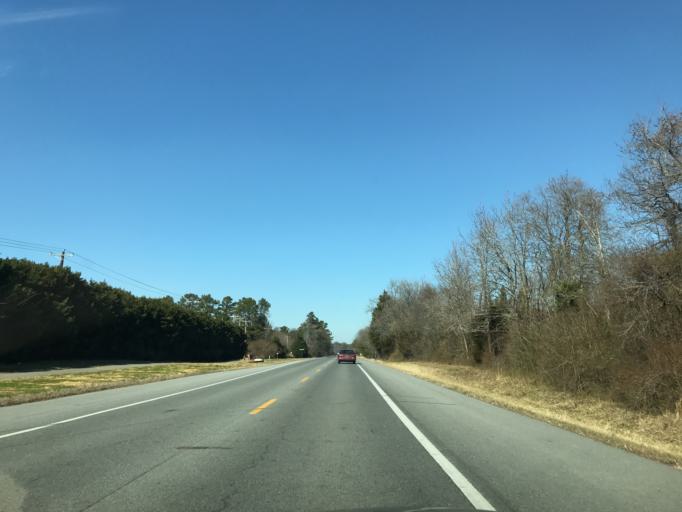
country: US
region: Maryland
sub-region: Queen Anne's County
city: Stevensville
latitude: 38.9124
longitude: -76.3526
